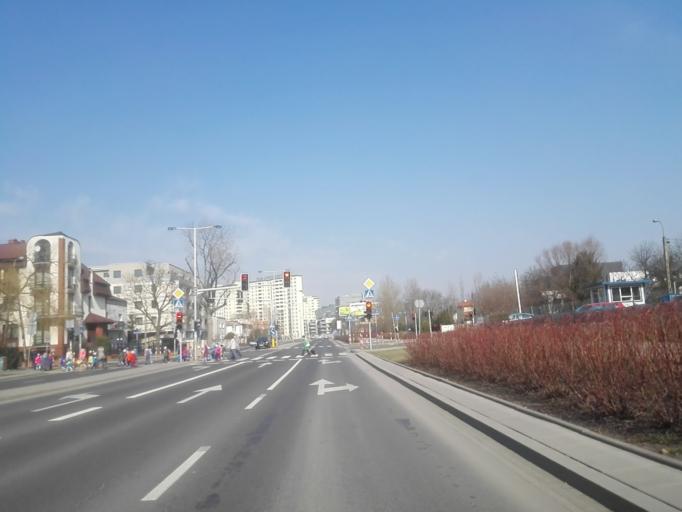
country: PL
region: Masovian Voivodeship
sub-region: Warszawa
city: Mokotow
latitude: 52.1756
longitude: 21.0267
